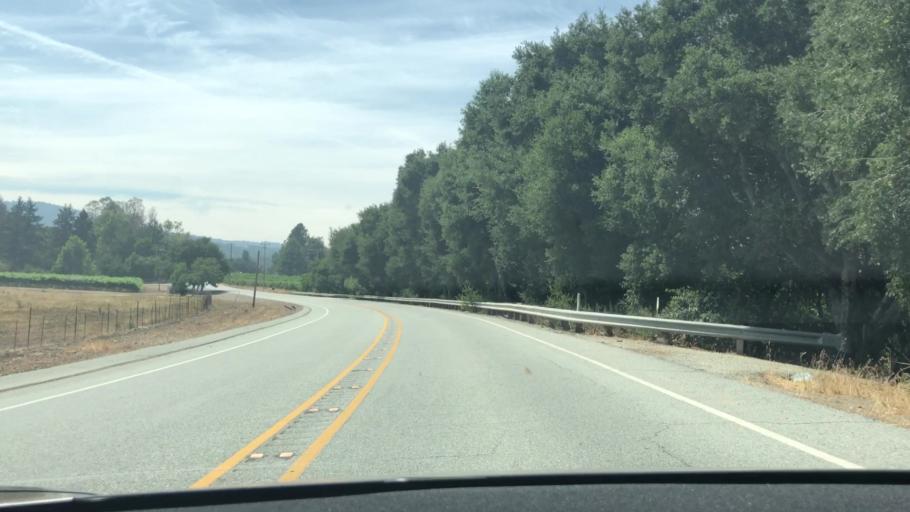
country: US
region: California
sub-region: Santa Clara County
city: Gilroy
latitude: 37.0131
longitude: -121.6324
